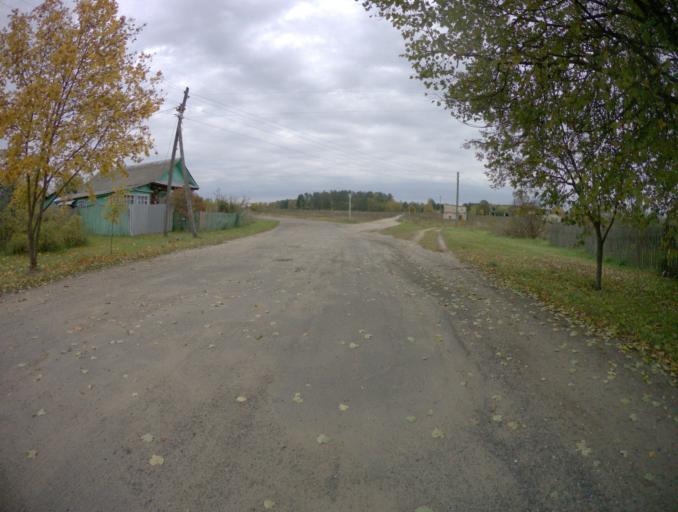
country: RU
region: Vladimir
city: Mstera
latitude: 56.3478
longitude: 41.7448
